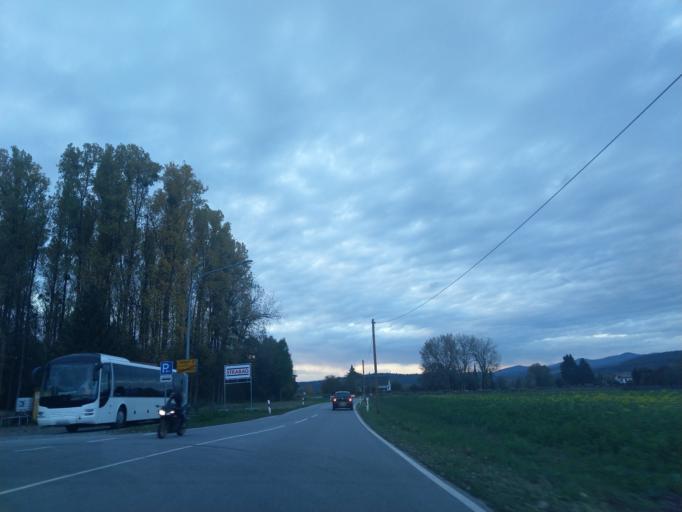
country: DE
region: Bavaria
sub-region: Lower Bavaria
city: Niederalteich
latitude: 48.7686
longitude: 13.0194
